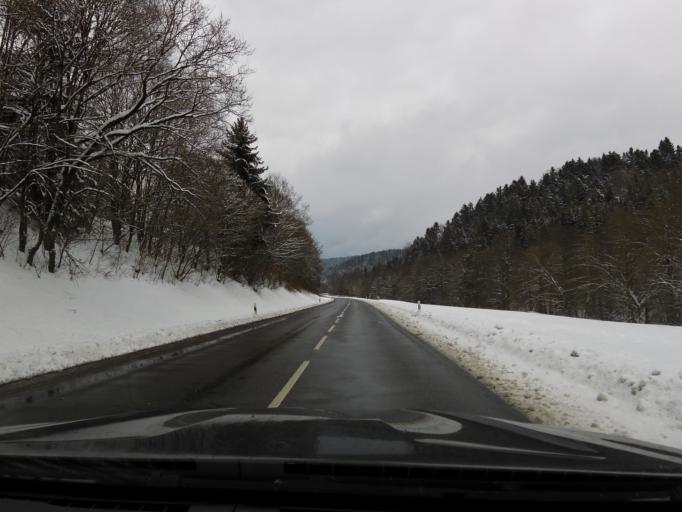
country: DE
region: Bavaria
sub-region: Lower Bavaria
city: Innernzell
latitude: 48.8503
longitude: 13.3076
